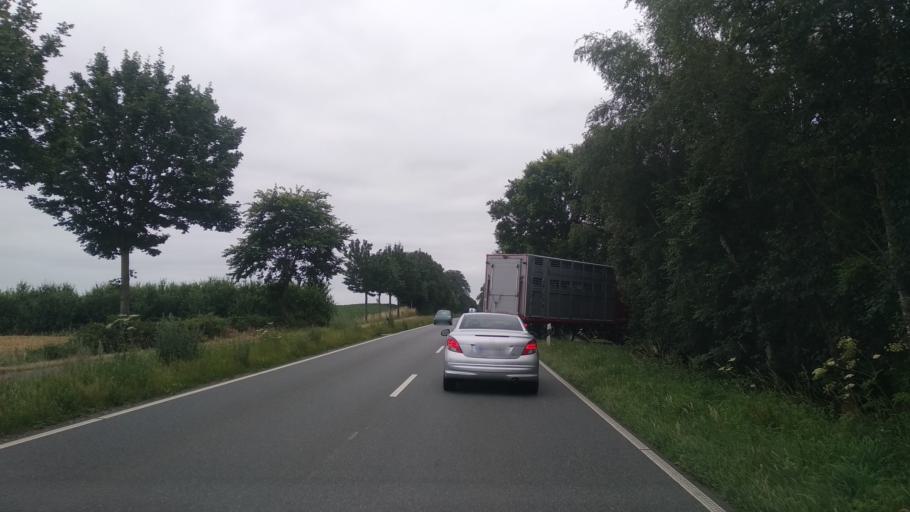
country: DE
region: Schleswig-Holstein
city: Ringsberg
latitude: 54.8030
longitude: 9.6115
